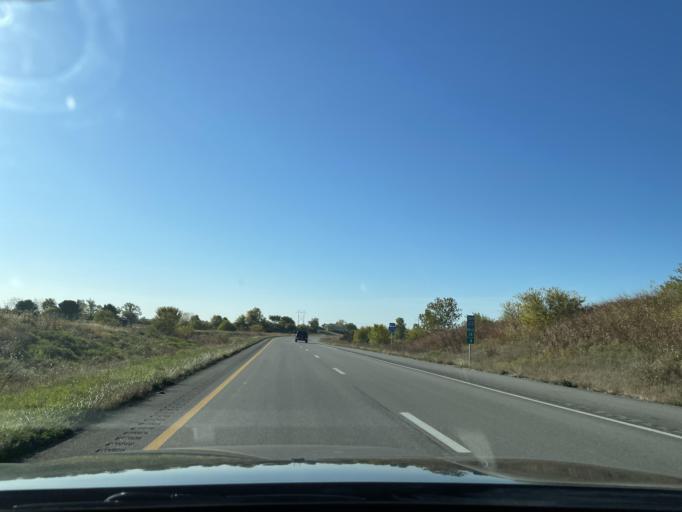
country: US
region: Missouri
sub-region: Andrew County
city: Country Club Village
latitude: 39.8831
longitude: -94.8581
